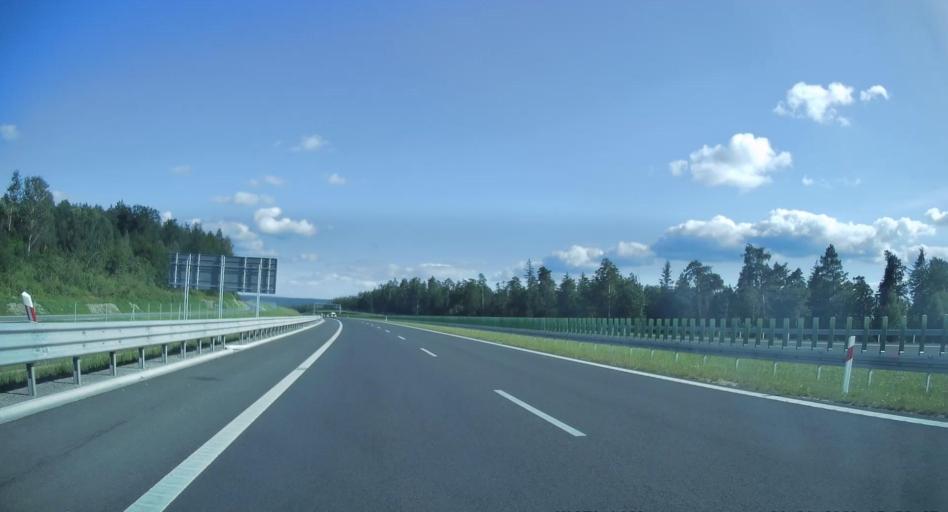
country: PL
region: Swietokrzyskie
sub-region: Powiat skarzyski
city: Skarzysko-Kamienna
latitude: 51.1332
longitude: 20.8344
